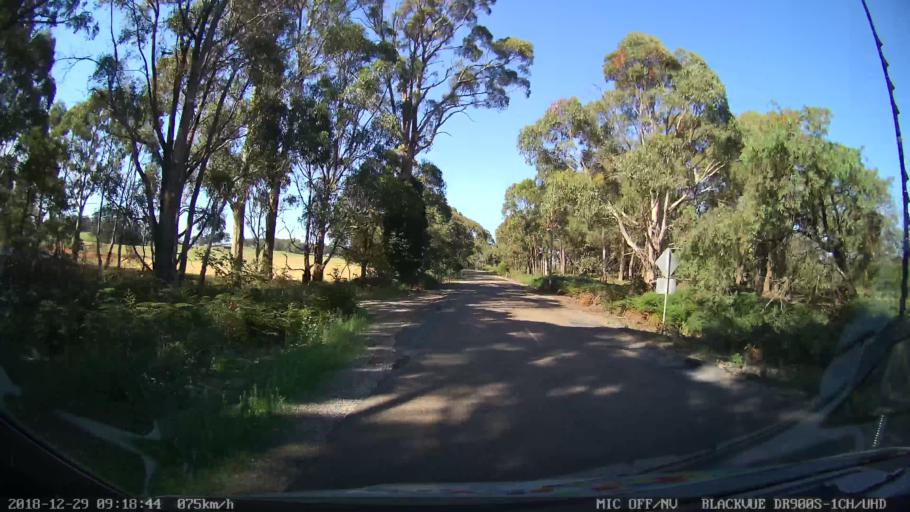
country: AU
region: New South Wales
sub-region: Upper Lachlan Shire
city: Crookwell
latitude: -34.4746
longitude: 149.4336
